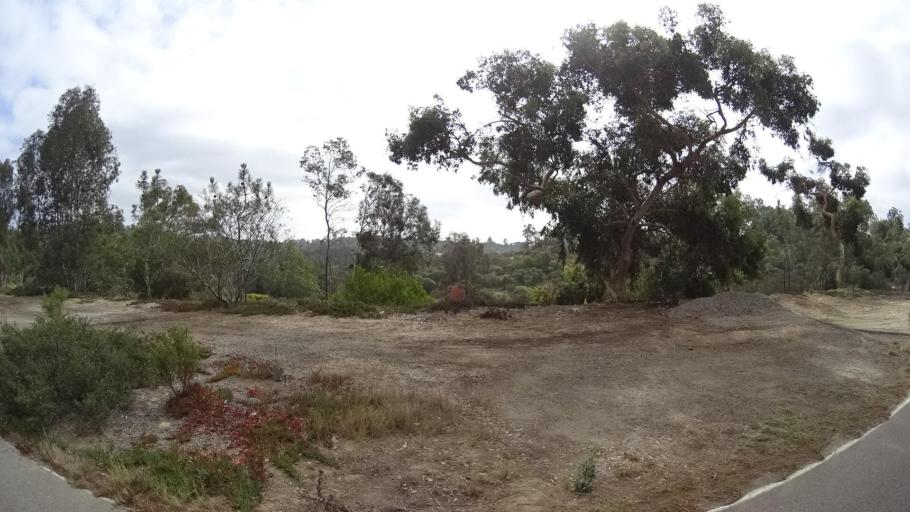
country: US
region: California
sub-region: San Diego County
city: Solana Beach
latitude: 33.0006
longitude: -117.2387
